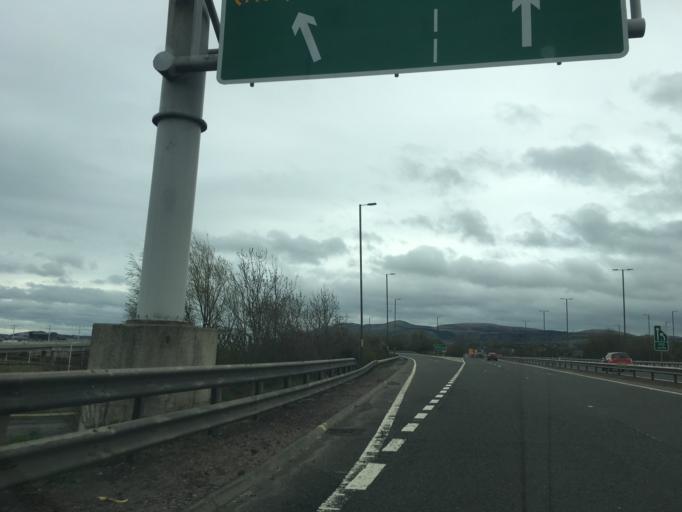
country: GB
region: Scotland
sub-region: Edinburgh
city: Currie
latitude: 55.9283
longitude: -3.3164
